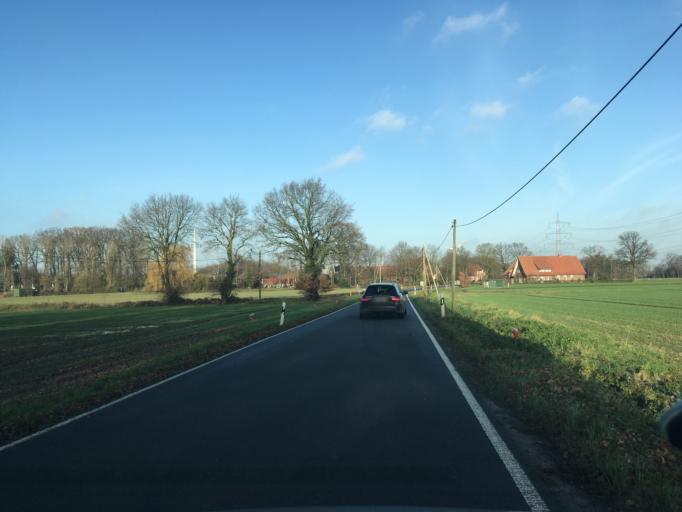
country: DE
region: North Rhine-Westphalia
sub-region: Regierungsbezirk Munster
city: Velen
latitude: 51.9307
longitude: 6.9636
